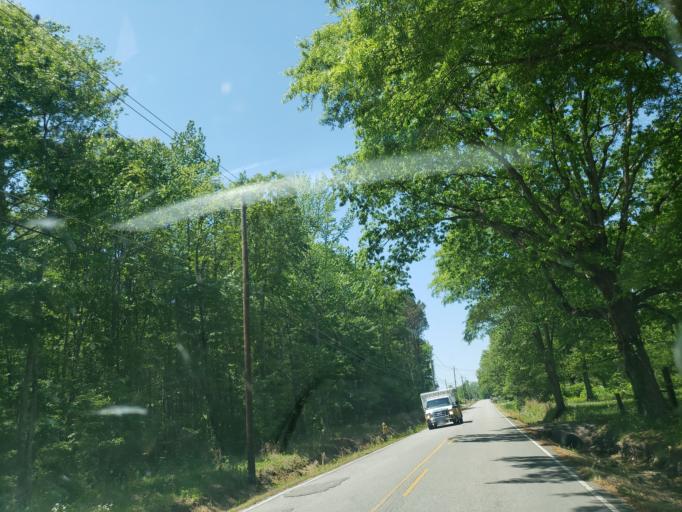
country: US
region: Alabama
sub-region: Madison County
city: Hazel Green
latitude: 34.9623
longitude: -86.6896
